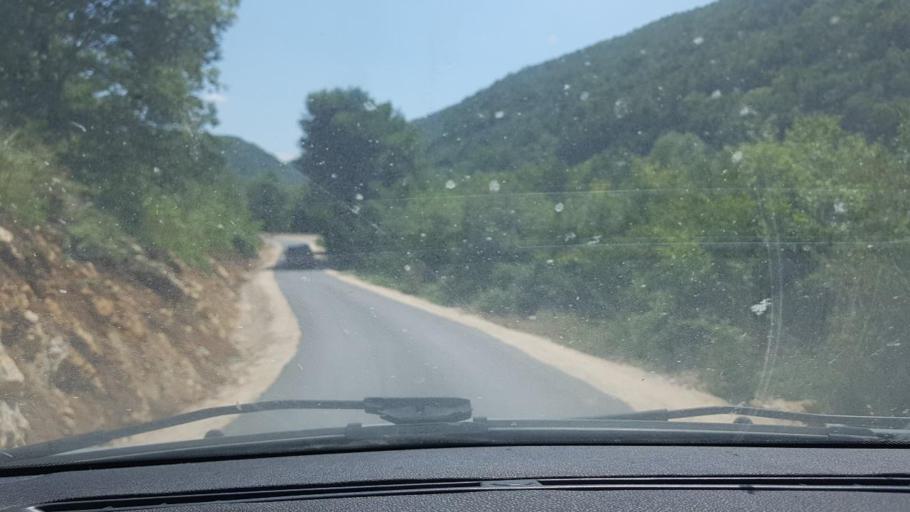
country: BA
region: Federation of Bosnia and Herzegovina
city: Orasac
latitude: 44.6437
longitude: 16.0374
